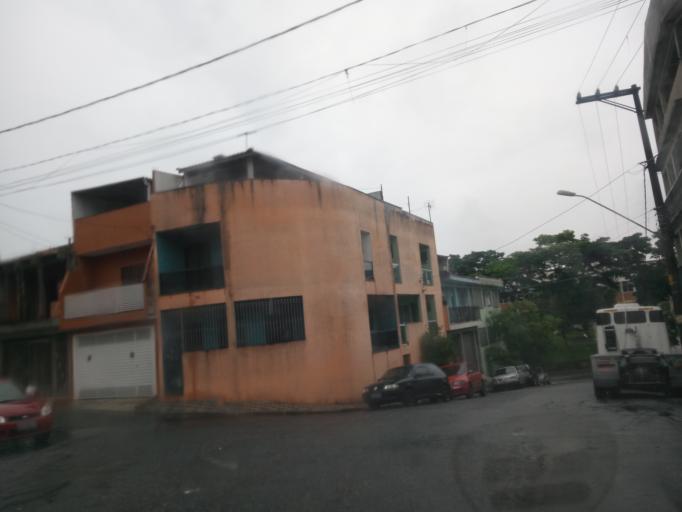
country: BR
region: Sao Paulo
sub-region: Sao Bernardo Do Campo
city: Sao Bernardo do Campo
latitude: -23.7282
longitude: -46.5906
